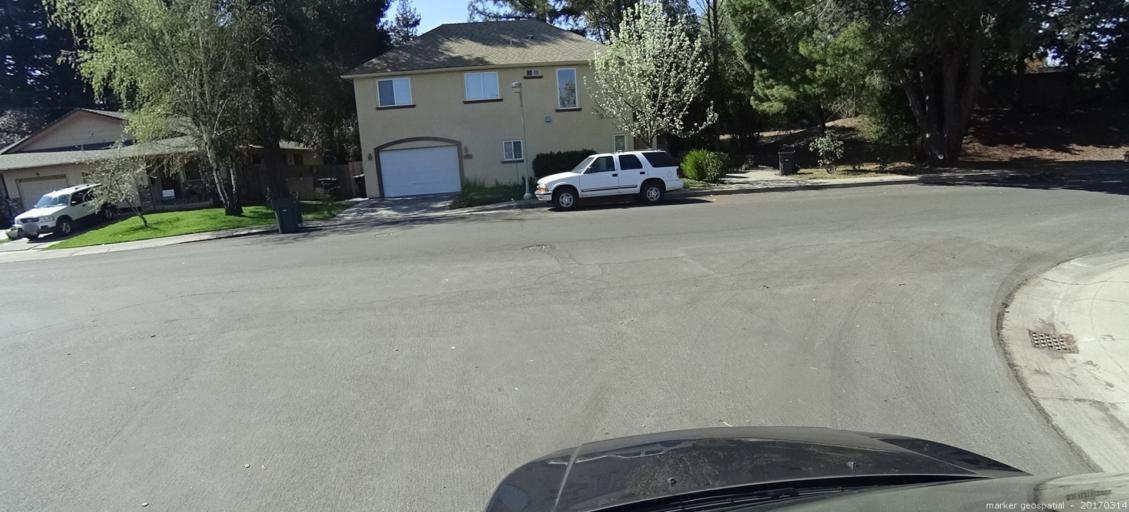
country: US
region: California
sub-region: Yolo County
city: West Sacramento
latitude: 38.5174
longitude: -121.5208
